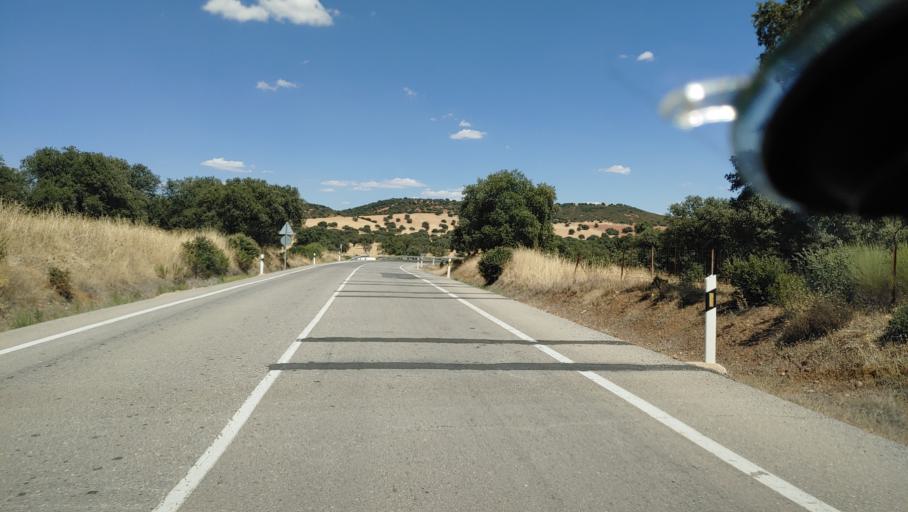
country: ES
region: Castille-La Mancha
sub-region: Provincia de Ciudad Real
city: Saceruela
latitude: 39.0163
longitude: -4.4807
